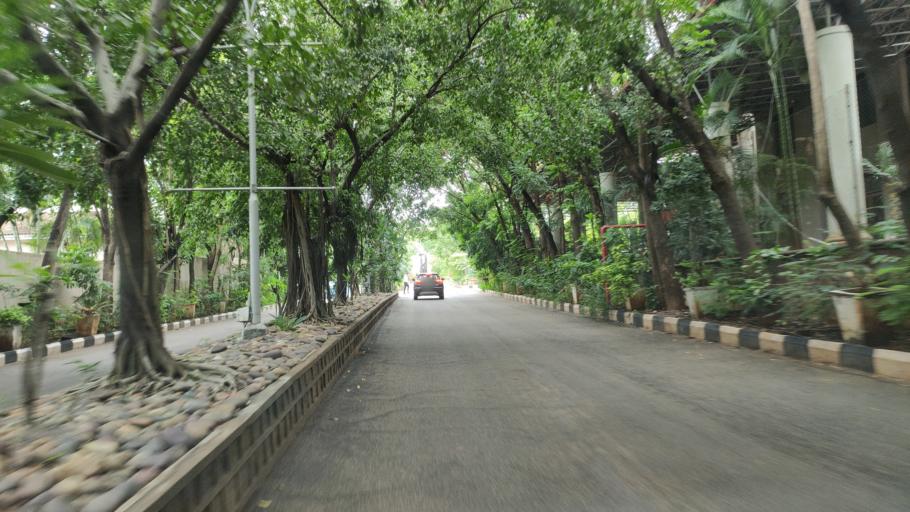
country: IN
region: Telangana
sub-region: Rangareddi
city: Secunderabad
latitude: 17.5795
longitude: 78.6013
